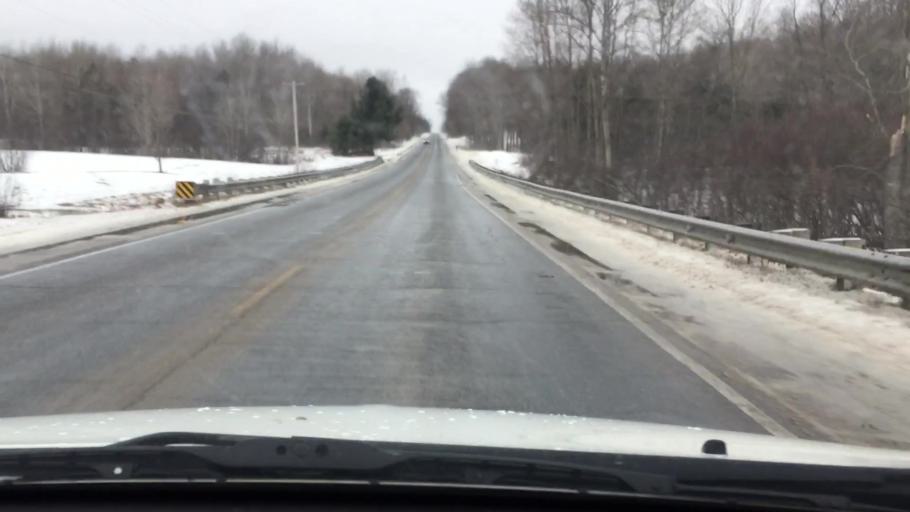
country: US
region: Michigan
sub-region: Wexford County
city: Cadillac
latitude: 44.1020
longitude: -85.4443
